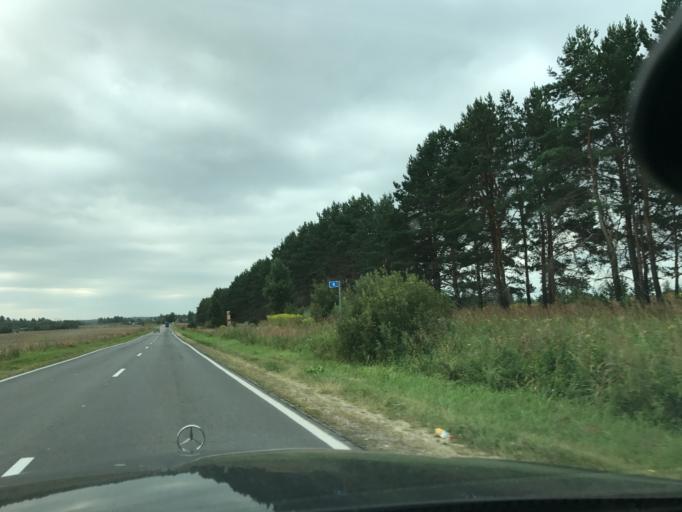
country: RU
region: Vladimir
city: Galitsy
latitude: 56.1679
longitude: 42.8130
